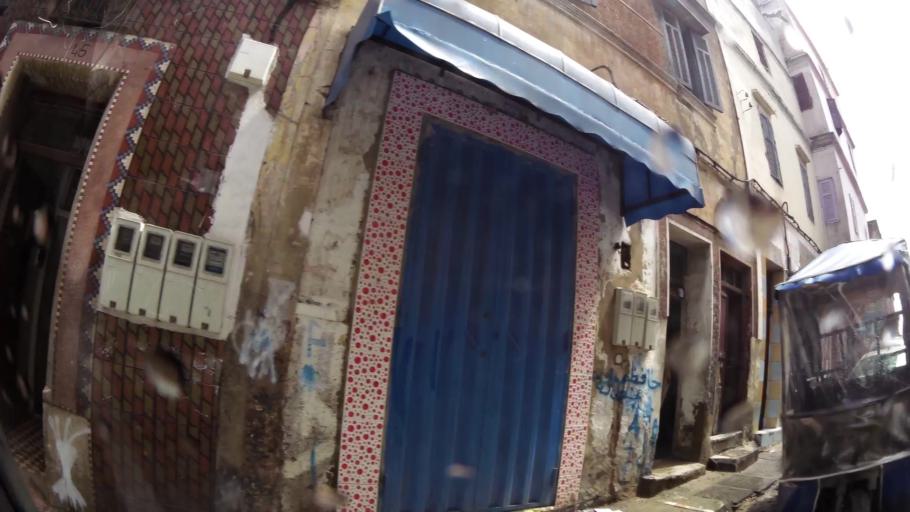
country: MA
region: Grand Casablanca
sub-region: Casablanca
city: Casablanca
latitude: 33.5740
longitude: -7.5954
